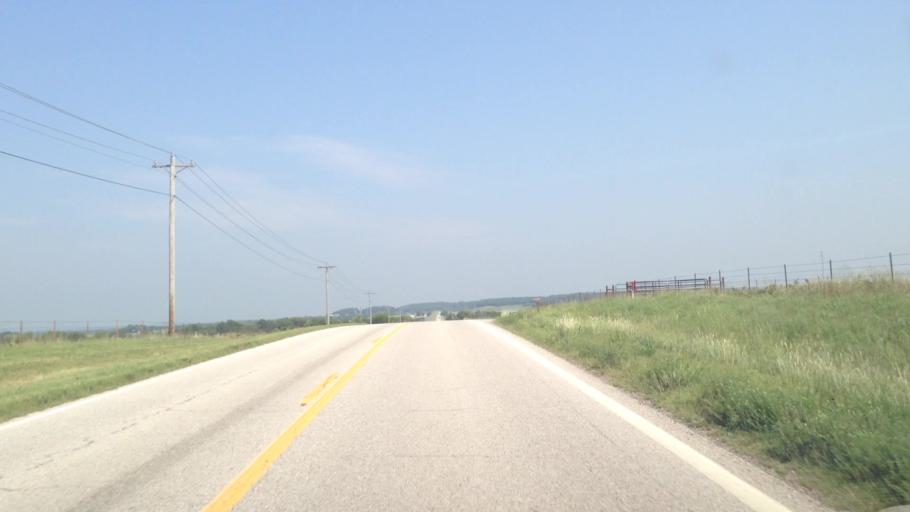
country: US
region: Oklahoma
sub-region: Craig County
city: Vinita
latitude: 36.7399
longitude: -95.1435
